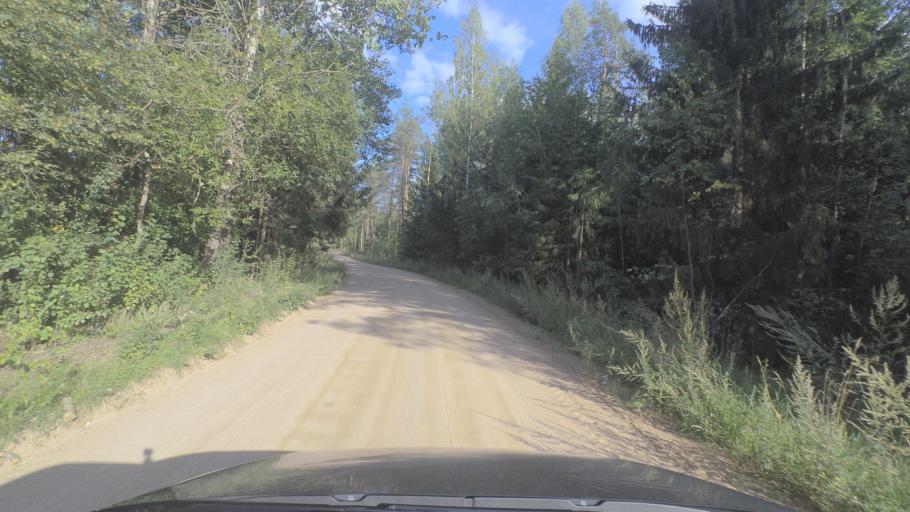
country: LT
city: Pabrade
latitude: 55.1479
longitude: 25.7551
